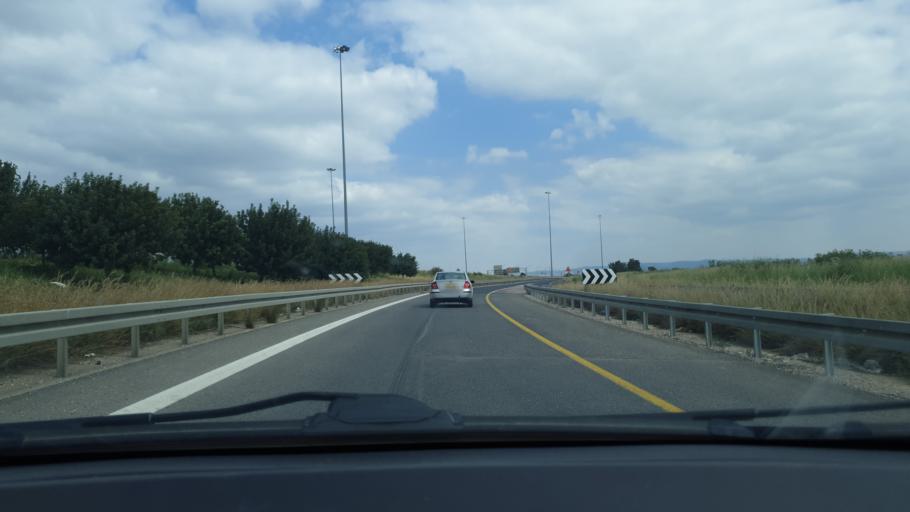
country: IL
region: Central District
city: Lod
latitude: 31.9093
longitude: 34.9006
